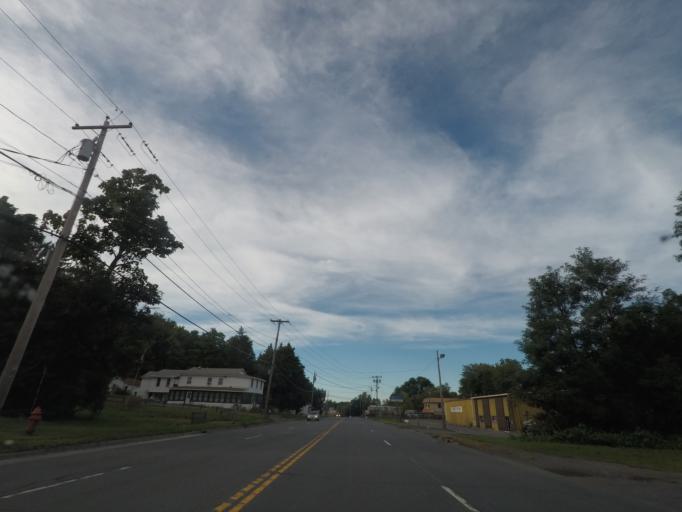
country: US
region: New York
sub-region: Rensselaer County
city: East Greenbush
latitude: 42.5681
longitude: -73.6846
